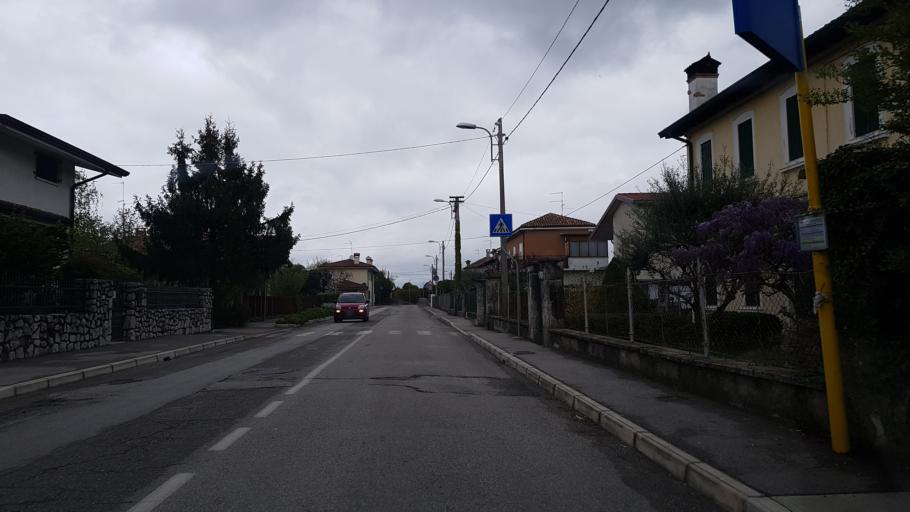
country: IT
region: Friuli Venezia Giulia
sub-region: Provincia di Gorizia
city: Turriaco
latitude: 45.8241
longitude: 13.4431
